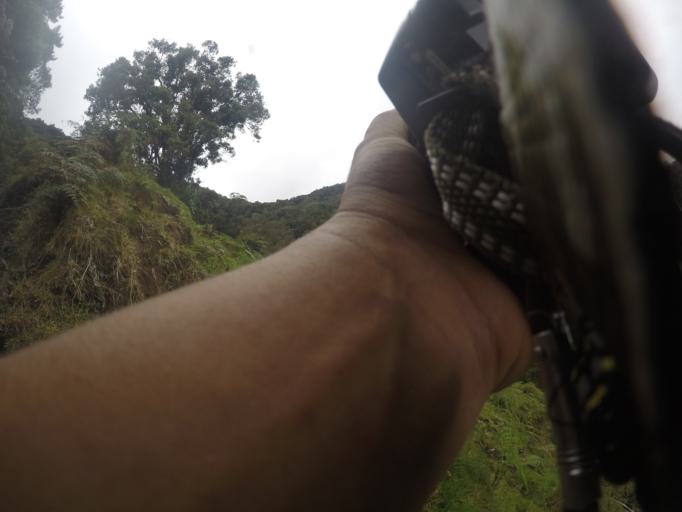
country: CO
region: Tolima
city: Cajamarca
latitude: 4.5336
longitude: -75.3507
